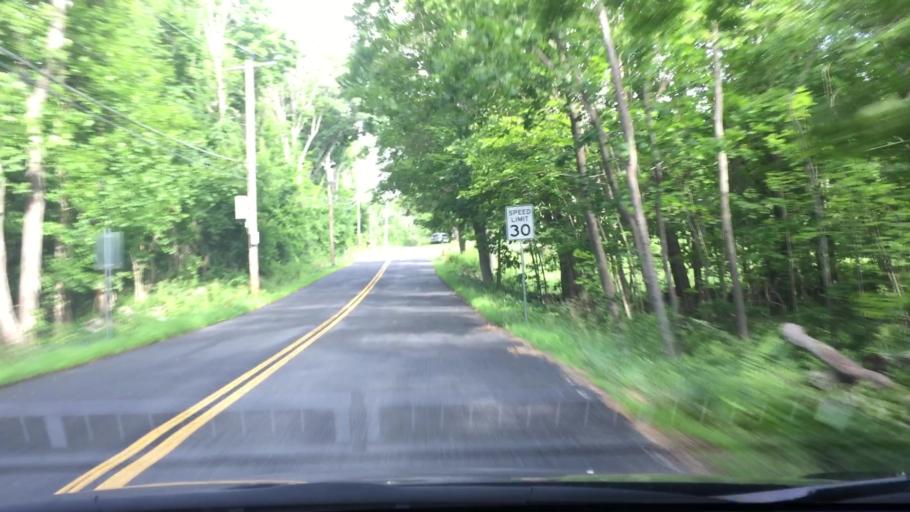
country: US
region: Massachusetts
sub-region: Middlesex County
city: Acton
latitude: 42.5009
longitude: -71.4399
